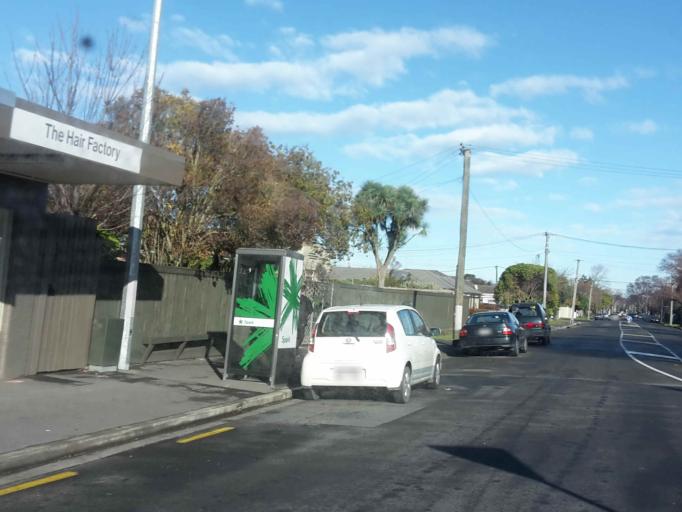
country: NZ
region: Canterbury
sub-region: Christchurch City
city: Christchurch
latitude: -43.5036
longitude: 172.5939
